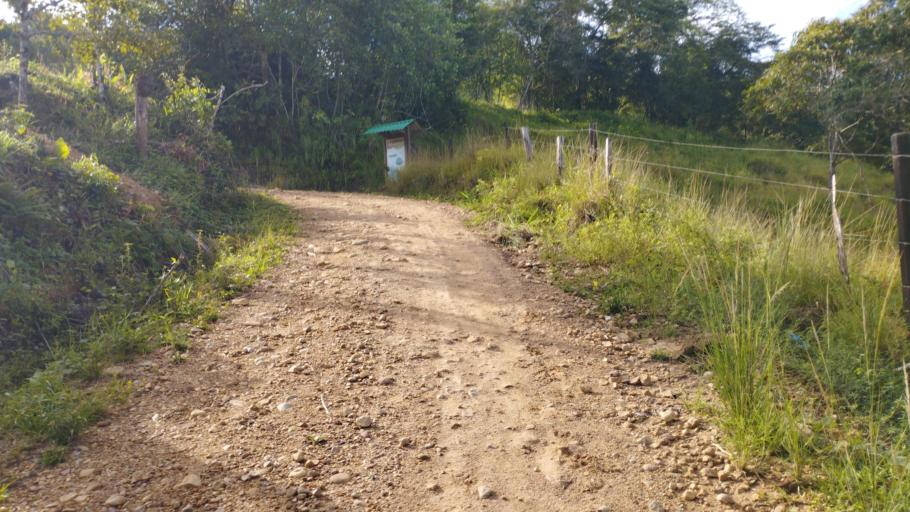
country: CO
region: Boyaca
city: San Luis de Gaceno
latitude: 4.8166
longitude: -73.1599
